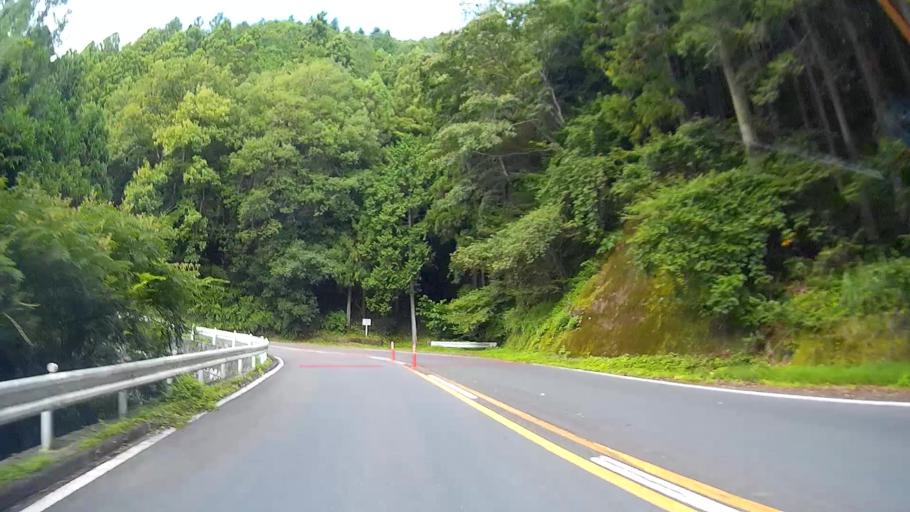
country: JP
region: Saitama
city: Chichibu
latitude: 35.9271
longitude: 139.1490
